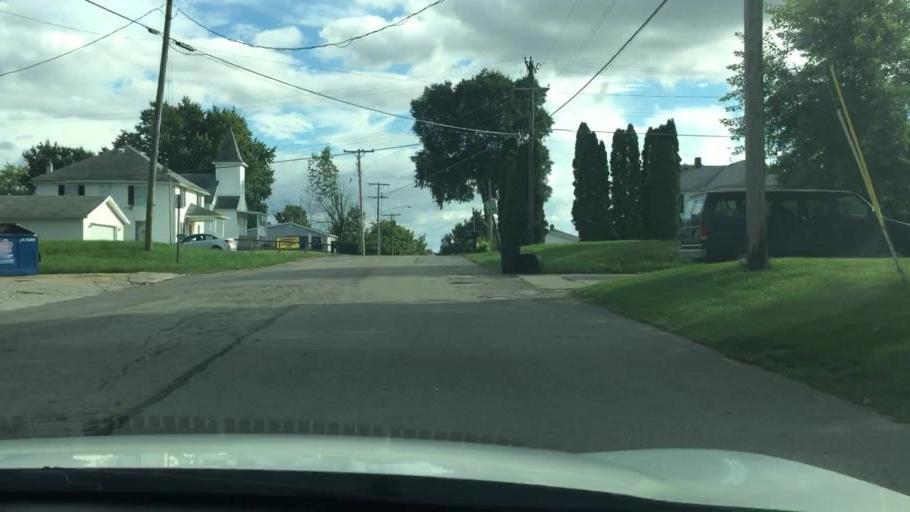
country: US
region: Ohio
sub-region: Champaign County
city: Mechanicsburg
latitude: 40.0823
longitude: -83.5655
